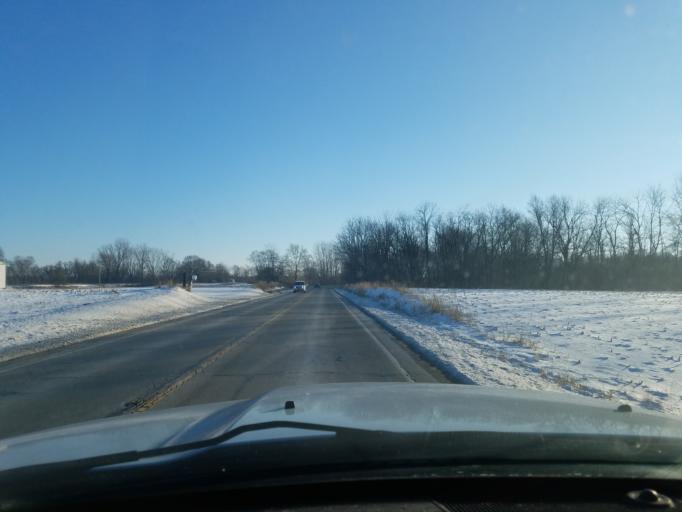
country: US
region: Indiana
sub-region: Noble County
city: Ligonier
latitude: 41.4591
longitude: -85.5169
